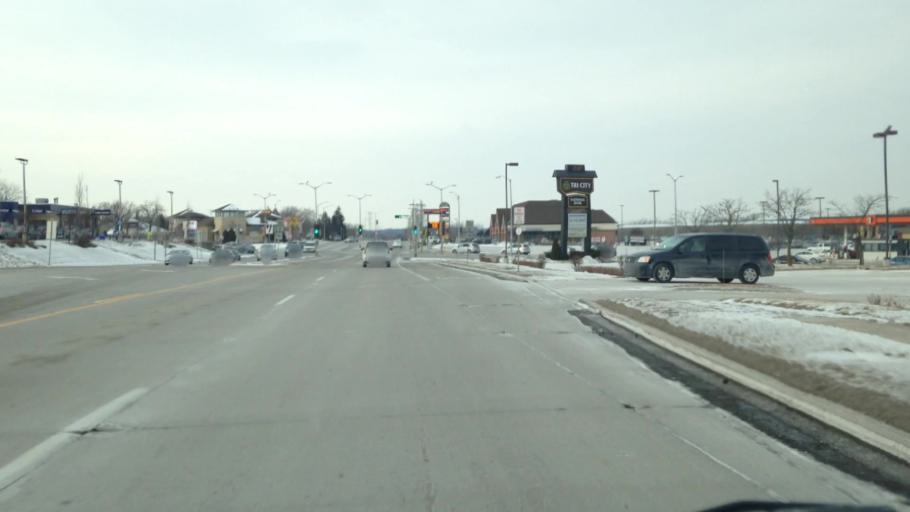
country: US
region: Wisconsin
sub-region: Waukesha County
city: Menomonee Falls
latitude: 43.1910
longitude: -88.1348
